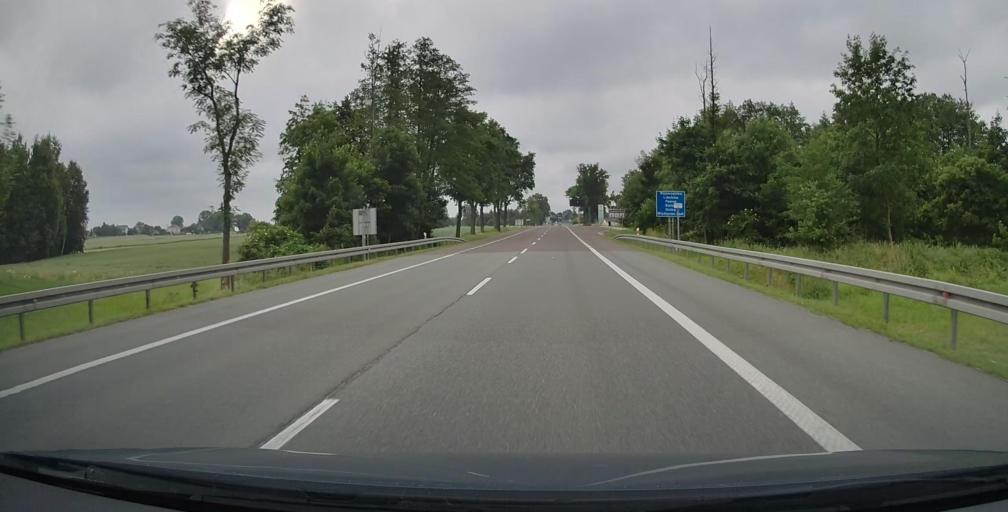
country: PL
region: Lublin Voivodeship
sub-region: Powiat lukowski
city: Trzebieszow
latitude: 52.0513
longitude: 22.6627
